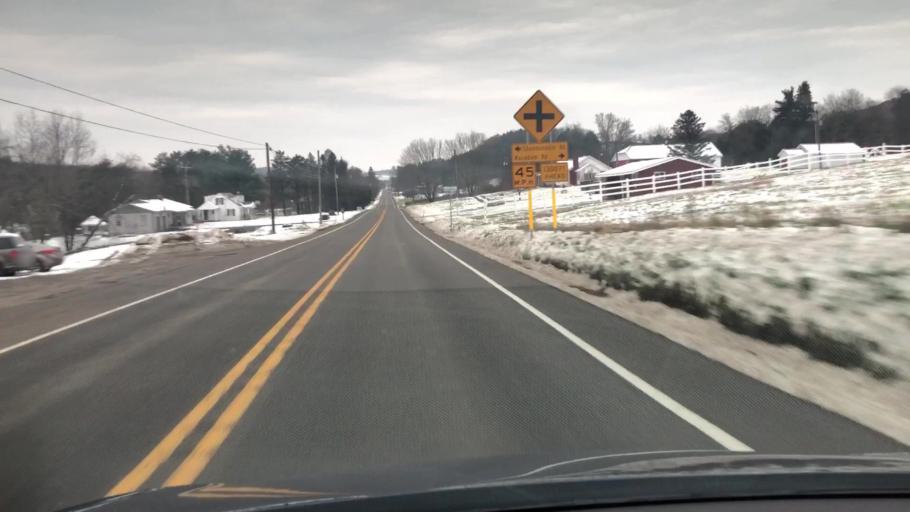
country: US
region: Pennsylvania
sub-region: Jefferson County
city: Brookville
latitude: 41.0777
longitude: -79.2346
